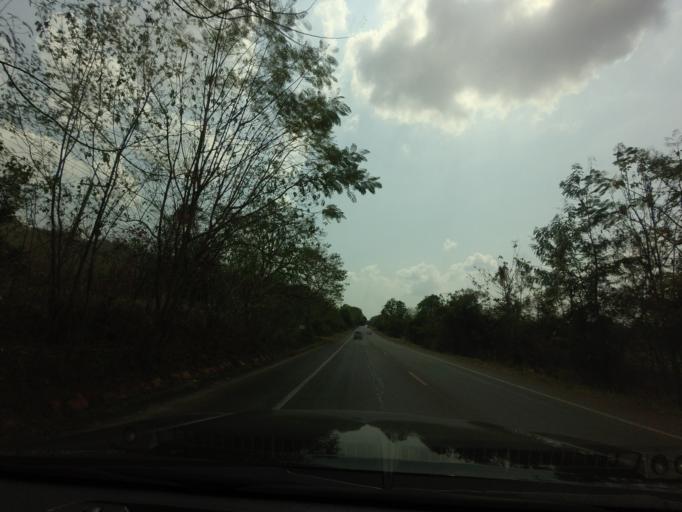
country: TH
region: Kanchanaburi
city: Sai Yok
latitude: 14.1532
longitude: 99.1414
